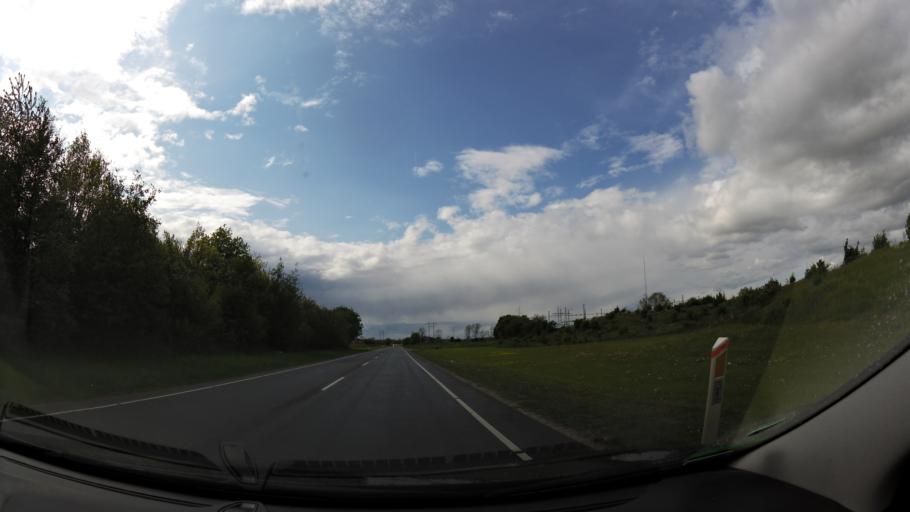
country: DK
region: South Denmark
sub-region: Nyborg Kommune
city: Nyborg
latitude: 55.3162
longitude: 10.7538
